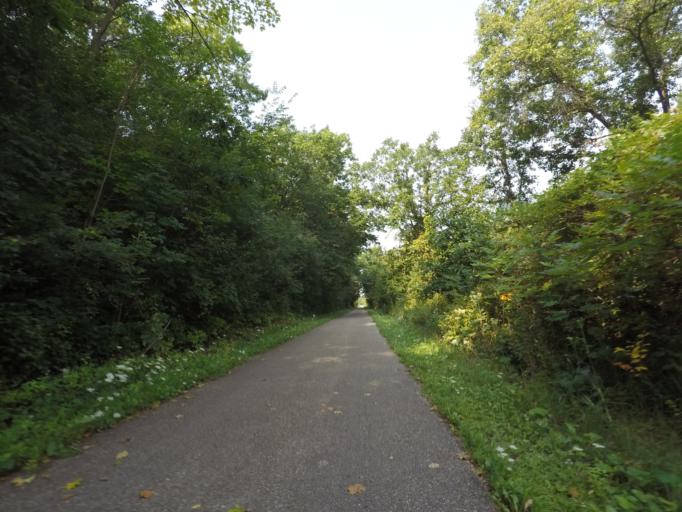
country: US
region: Wisconsin
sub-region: Waukesha County
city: Dousman
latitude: 43.0163
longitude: -88.4339
